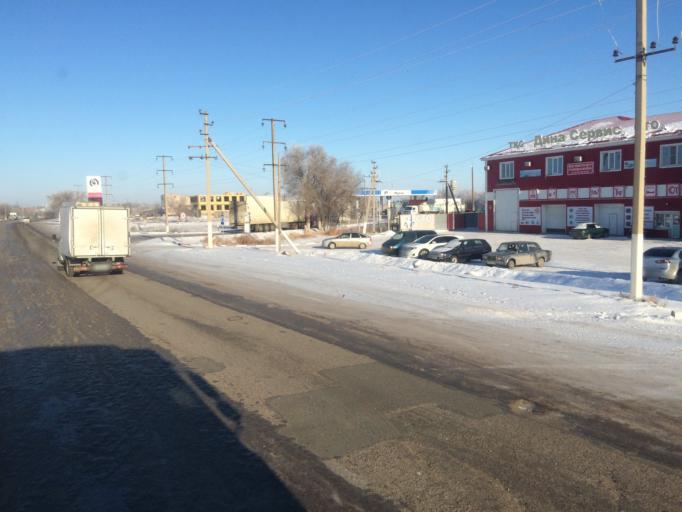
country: KZ
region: Aqtoebe
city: Aqtobe
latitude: 50.2459
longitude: 57.2507
